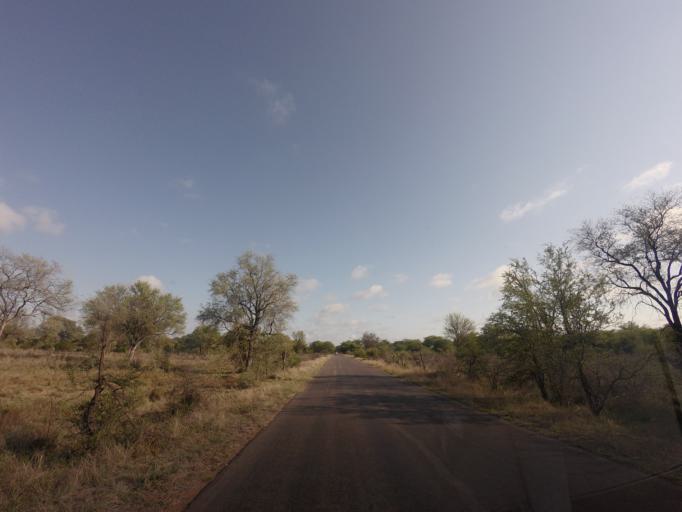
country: ZA
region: Mpumalanga
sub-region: Ehlanzeni District
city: Komatipoort
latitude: -25.2719
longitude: 31.8481
